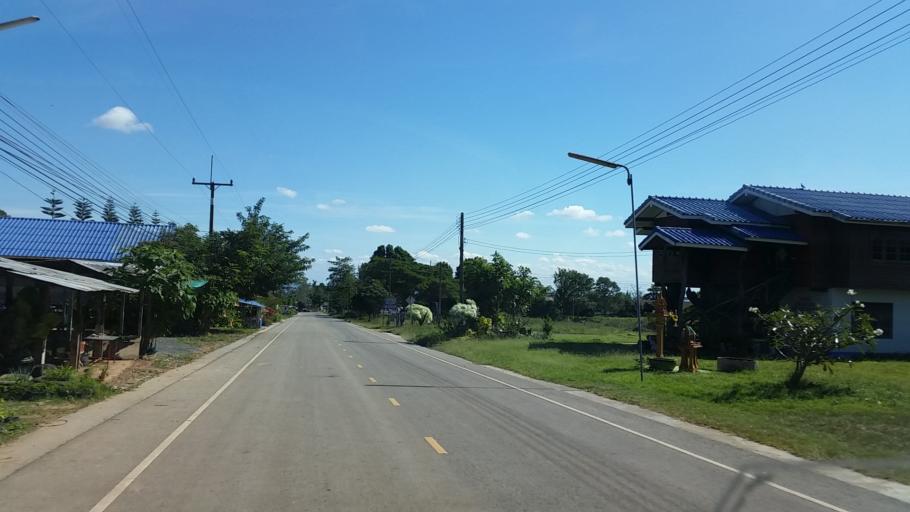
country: TH
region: Chaiyaphum
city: Sap Yai
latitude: 15.6280
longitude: 101.3969
